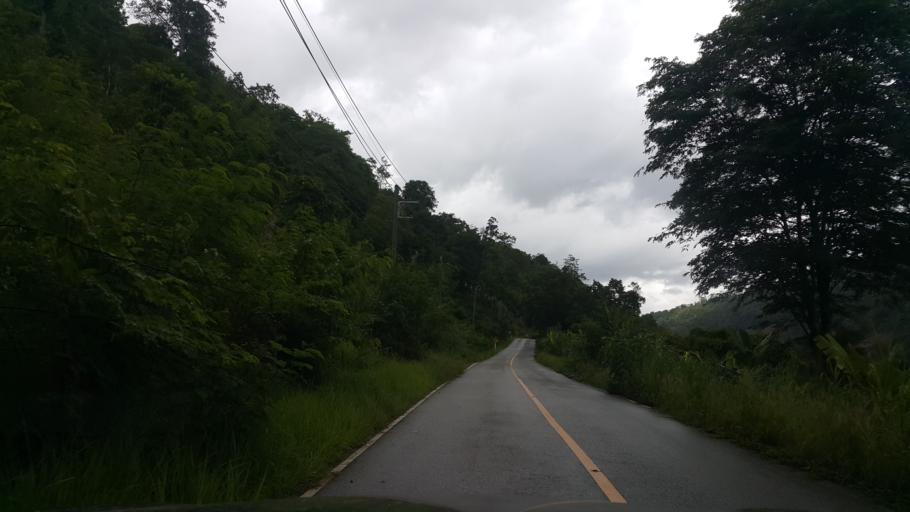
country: TH
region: Loei
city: Na Haeo
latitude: 17.4965
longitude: 100.8133
